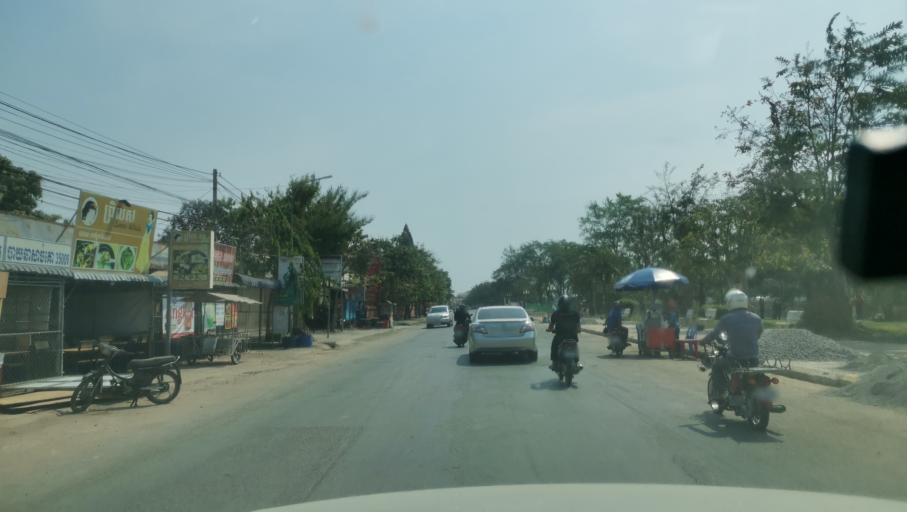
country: KH
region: Battambang
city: Battambang
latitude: 13.0939
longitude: 103.2005
